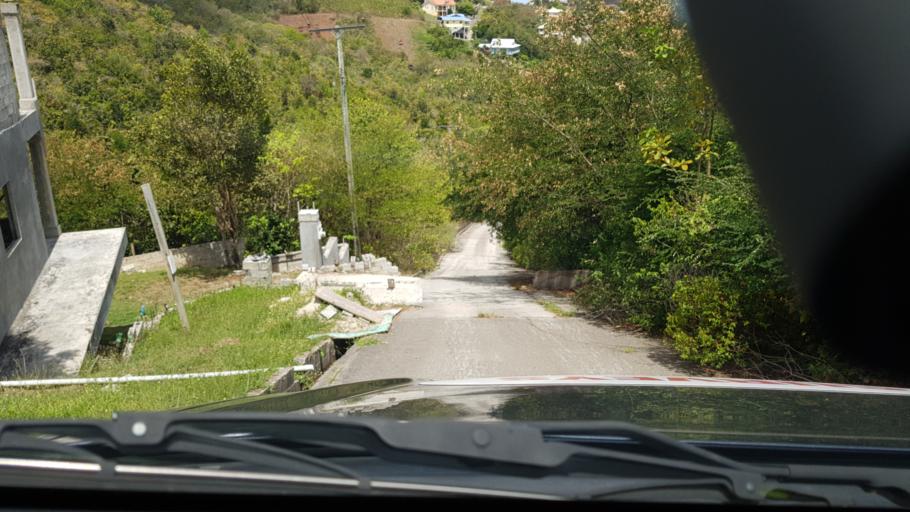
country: LC
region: Gros-Islet
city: Gros Islet
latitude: 14.0642
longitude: -60.9295
